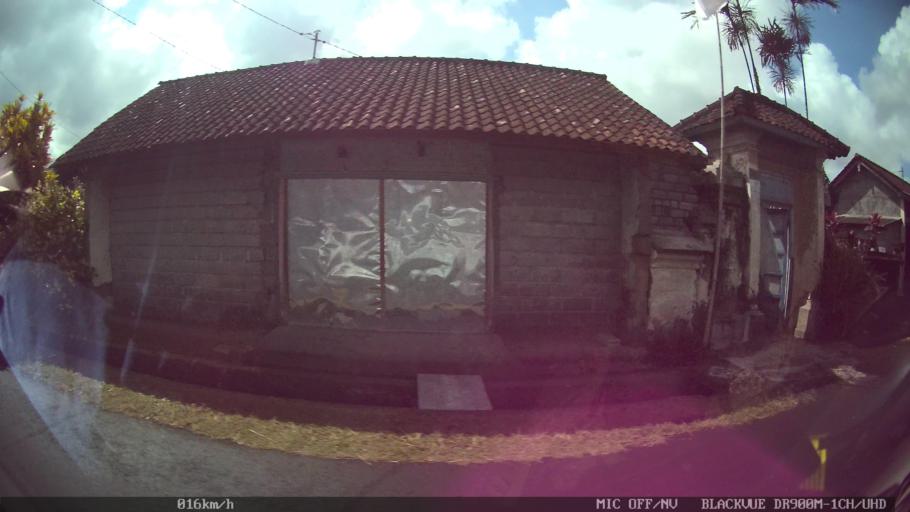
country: ID
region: Bali
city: Banjar Karangsuling
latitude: -8.6009
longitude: 115.2022
